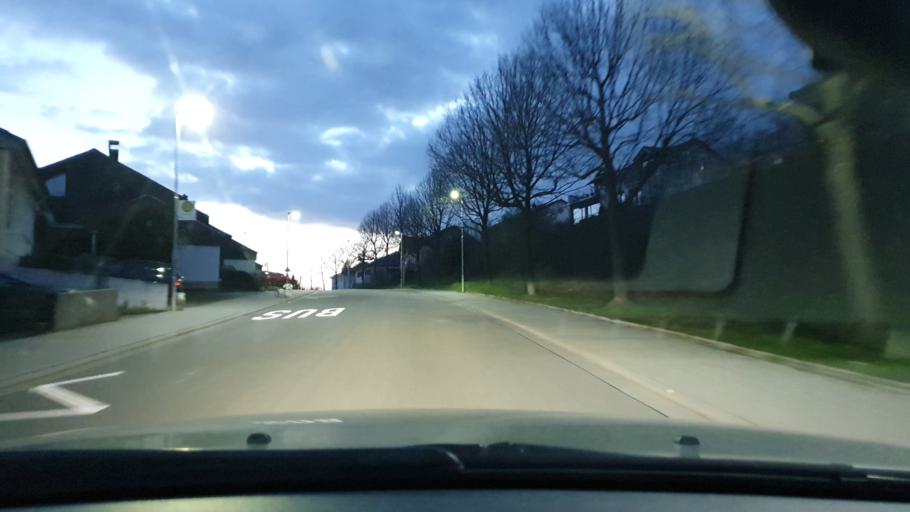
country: DE
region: Rheinland-Pfalz
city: Kaiserslautern
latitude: 49.4555
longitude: 7.7779
